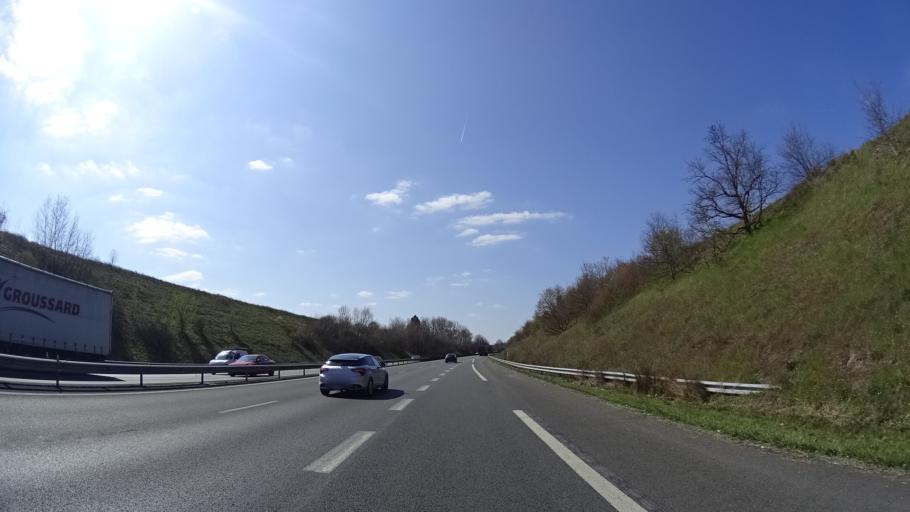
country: FR
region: Pays de la Loire
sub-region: Departement de Maine-et-Loire
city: Les Ponts-de-Ce
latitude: 47.3983
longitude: -0.5168
